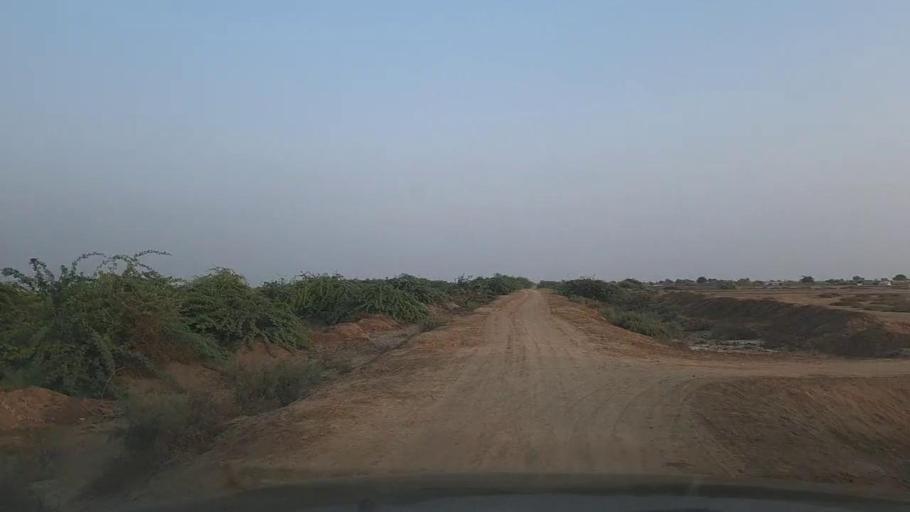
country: PK
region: Sindh
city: Jati
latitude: 24.5427
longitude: 68.3960
